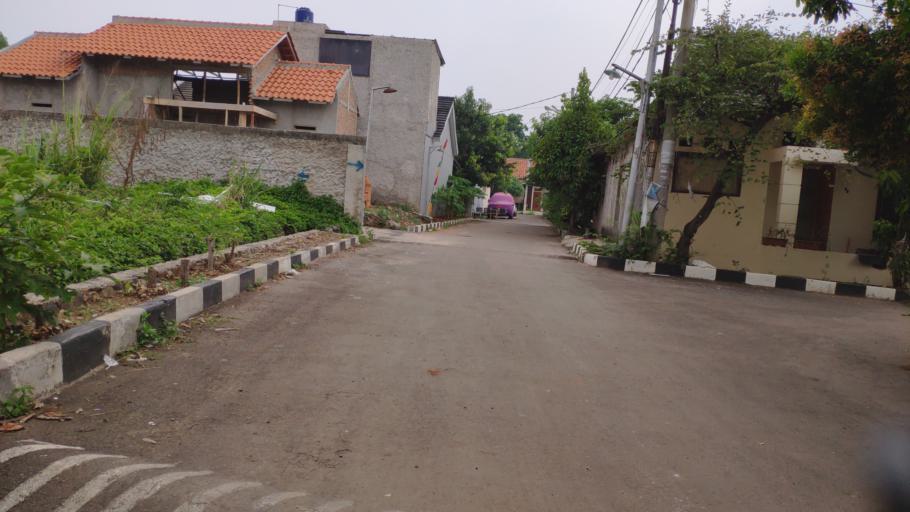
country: ID
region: West Java
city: Depok
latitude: -6.3781
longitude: 106.7973
